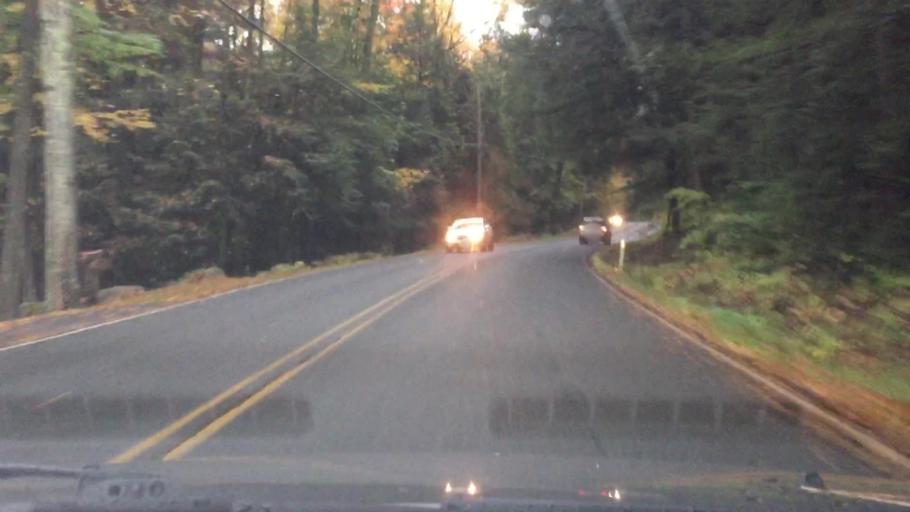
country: US
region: New Hampshire
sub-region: Cheshire County
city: Swanzey
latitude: 42.8985
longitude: -72.2848
